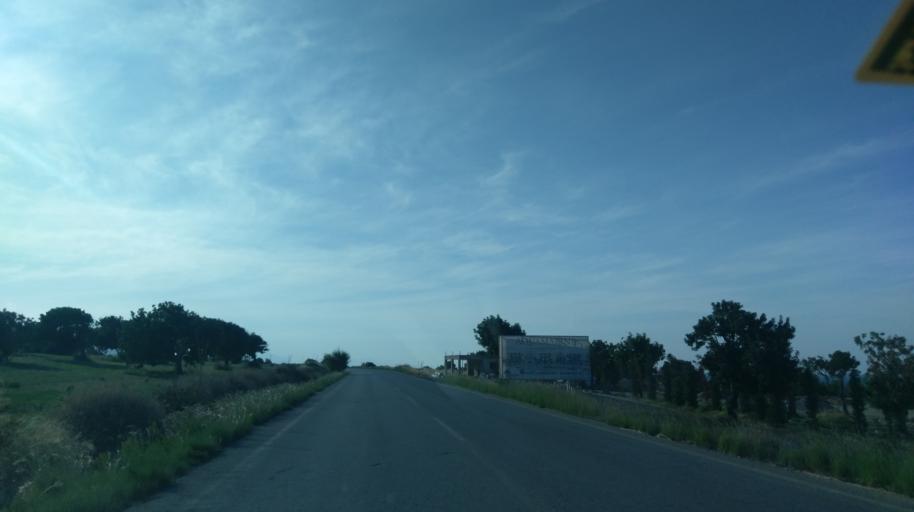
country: CY
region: Ammochostos
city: Lefkonoiko
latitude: 35.3626
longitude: 33.6750
